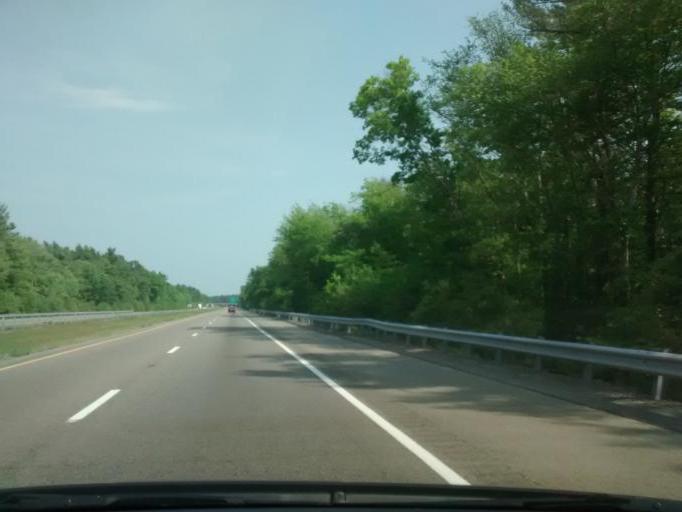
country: US
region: Massachusetts
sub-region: Plymouth County
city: Middleborough Center
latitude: 41.8550
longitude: -70.8698
